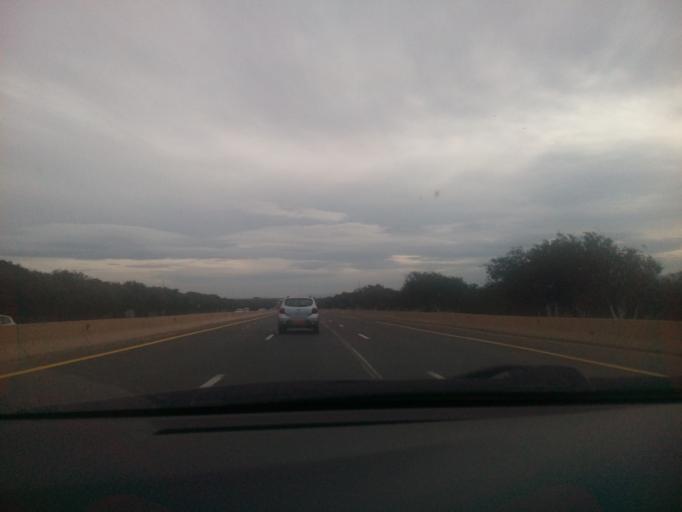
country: DZ
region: Oran
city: Es Senia
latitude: 35.5781
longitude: -0.5660
